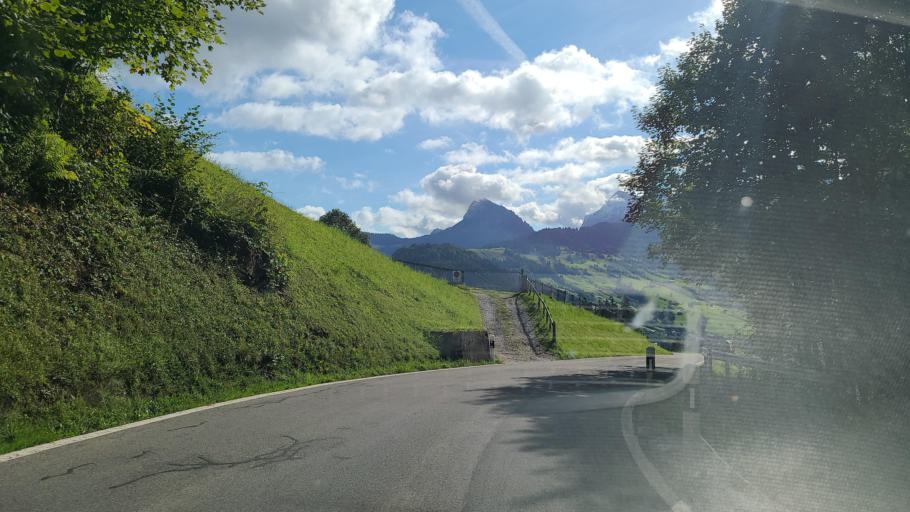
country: CH
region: Schwyz
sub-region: Bezirk March
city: Vorderthal
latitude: 47.1329
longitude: 8.8751
